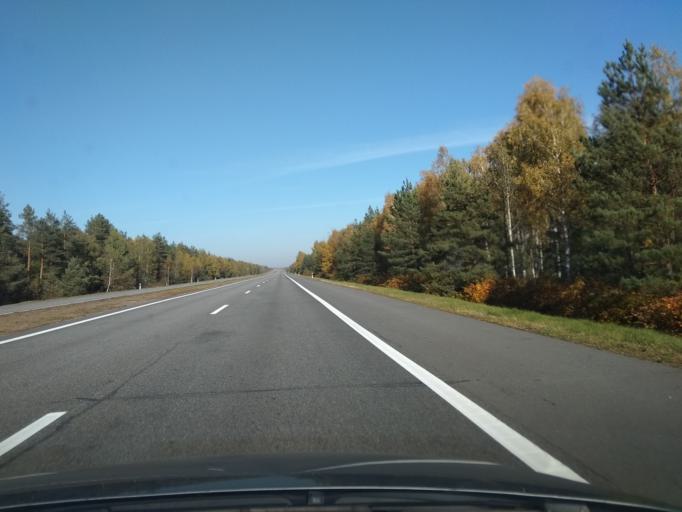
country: BY
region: Grodnenskaya
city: Zhyrovichy
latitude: 52.8966
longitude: 25.6730
